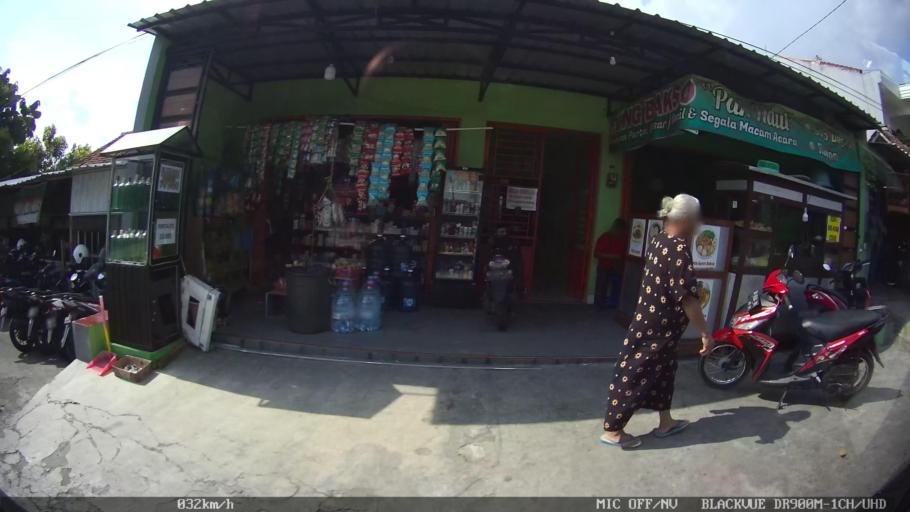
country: ID
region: Daerah Istimewa Yogyakarta
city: Kasihan
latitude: -7.8386
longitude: 110.3201
